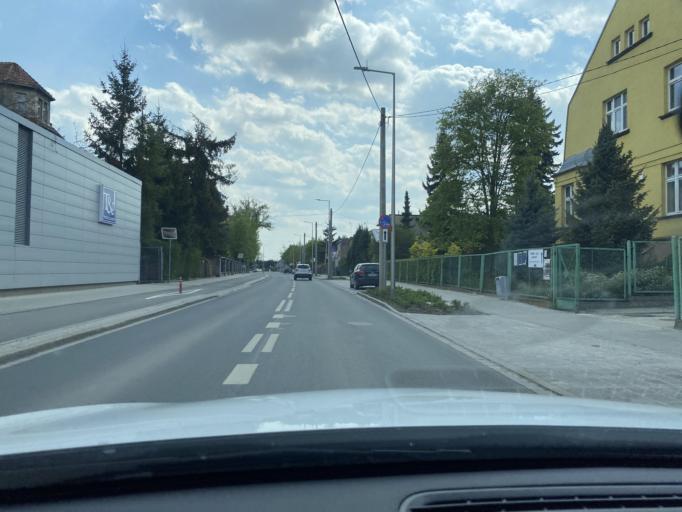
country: PL
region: Lower Silesian Voivodeship
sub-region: Powiat trzebnicki
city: Psary
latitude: 51.1437
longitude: 16.9879
